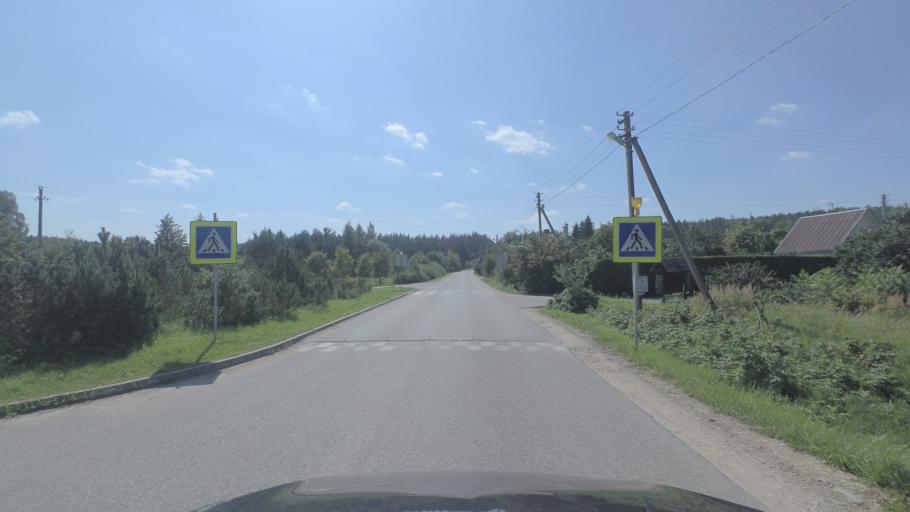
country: LT
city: Nemencine
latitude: 54.8289
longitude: 25.3640
